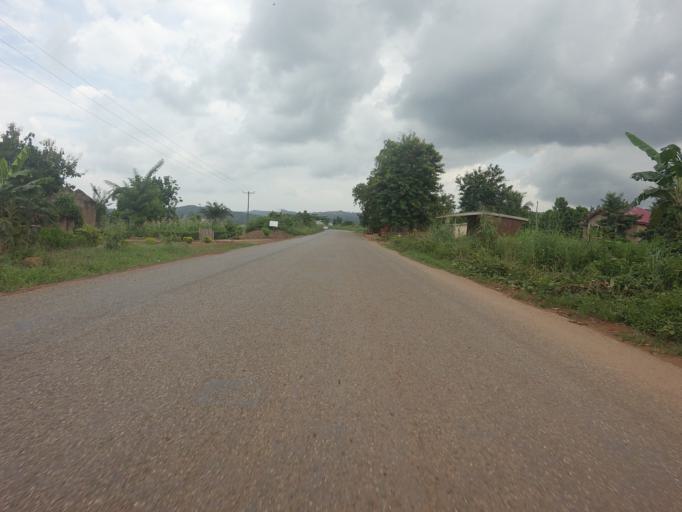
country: GH
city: Akropong
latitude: 5.9583
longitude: -0.1446
